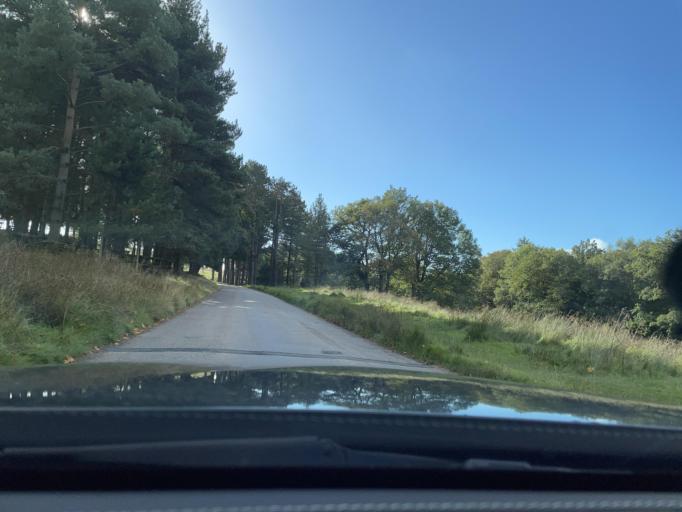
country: GB
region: England
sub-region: Cheshire East
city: Disley
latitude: 53.3518
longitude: -2.0547
